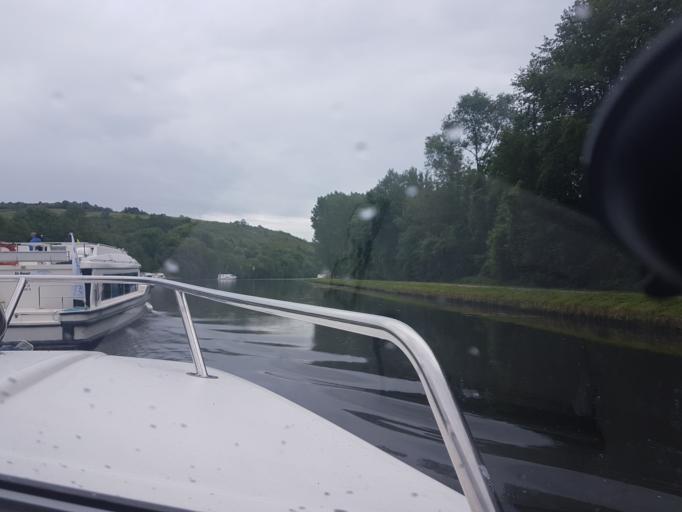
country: FR
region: Bourgogne
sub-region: Departement de l'Yonne
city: Champs-sur-Yonne
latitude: 47.7216
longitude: 3.6270
